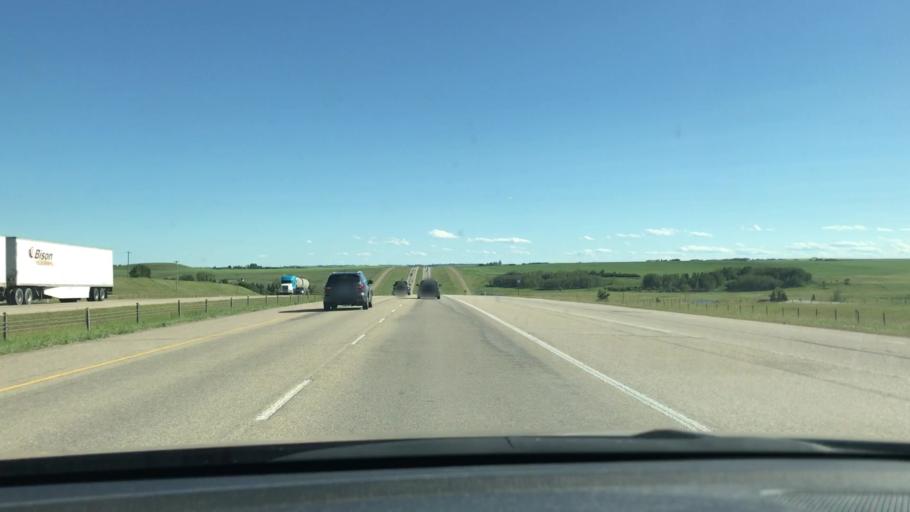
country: CA
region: Alberta
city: Carstairs
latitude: 51.5574
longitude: -114.0253
